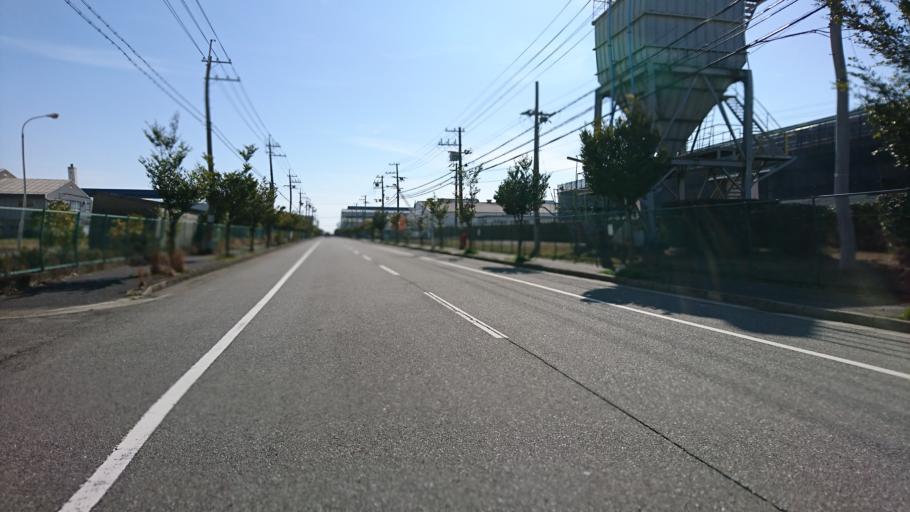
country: JP
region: Hyogo
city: Kakogawacho-honmachi
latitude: 34.7006
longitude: 134.8494
